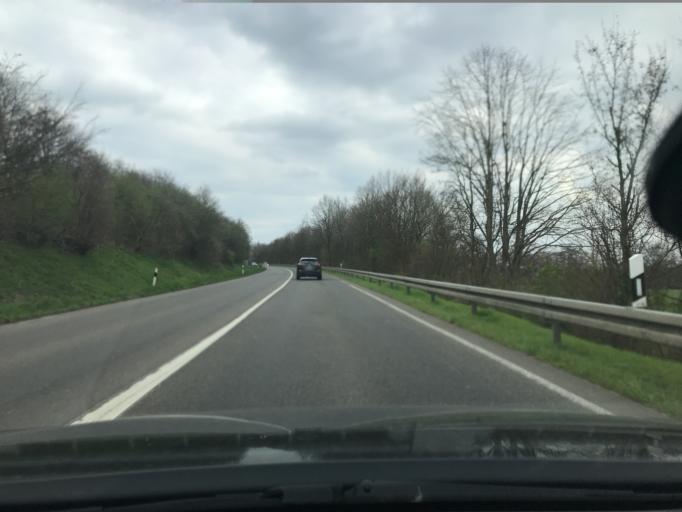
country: DE
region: North Rhine-Westphalia
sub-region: Regierungsbezirk Dusseldorf
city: Grefrath
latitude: 51.3324
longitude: 6.3314
